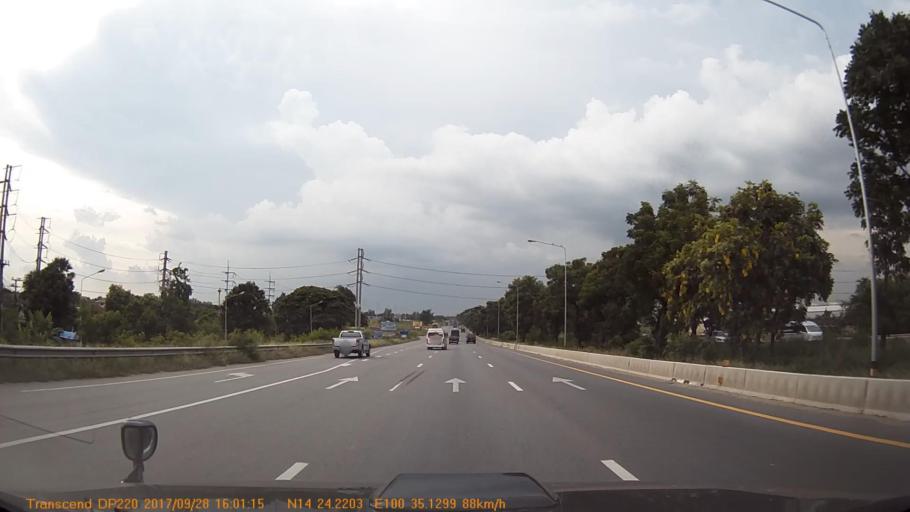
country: TH
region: Phra Nakhon Si Ayutthaya
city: Phra Nakhon Si Ayutthaya
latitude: 14.4038
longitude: 100.5854
